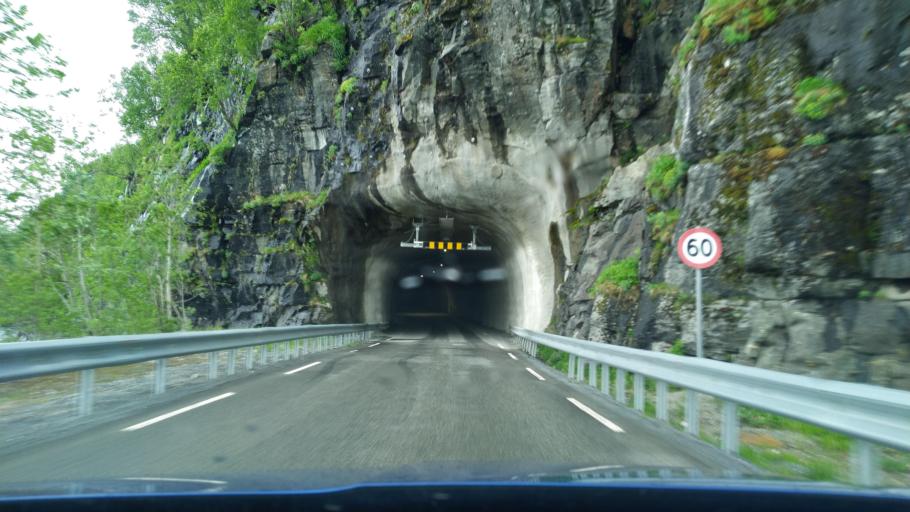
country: NO
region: Troms
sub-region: Lenvik
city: Finnsnes
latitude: 69.1452
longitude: 17.9491
